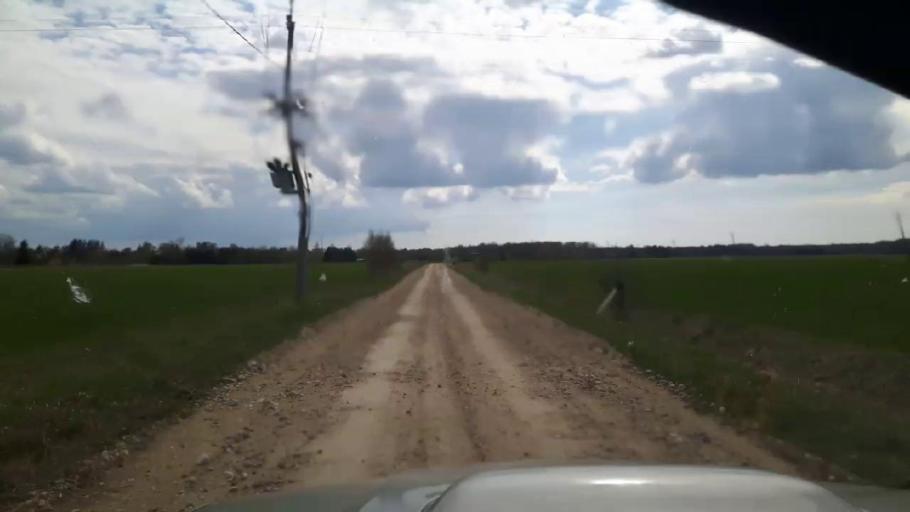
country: EE
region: Paernumaa
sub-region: Tootsi vald
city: Tootsi
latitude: 58.5108
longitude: 24.8441
